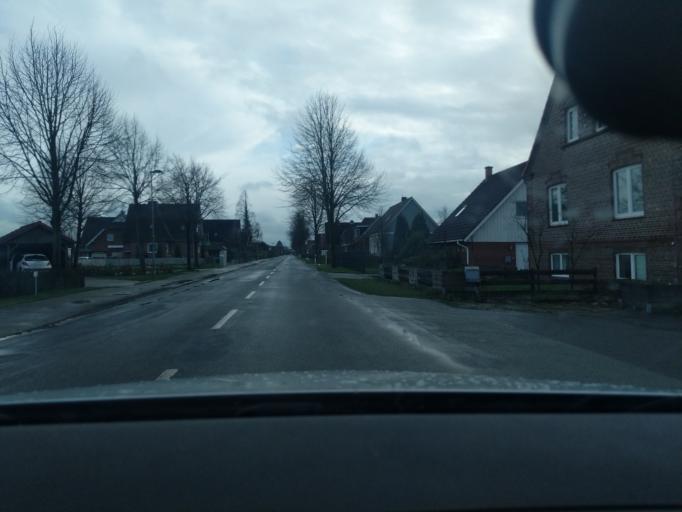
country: DE
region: Lower Saxony
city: Agathenburg
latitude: 53.5976
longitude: 9.5520
